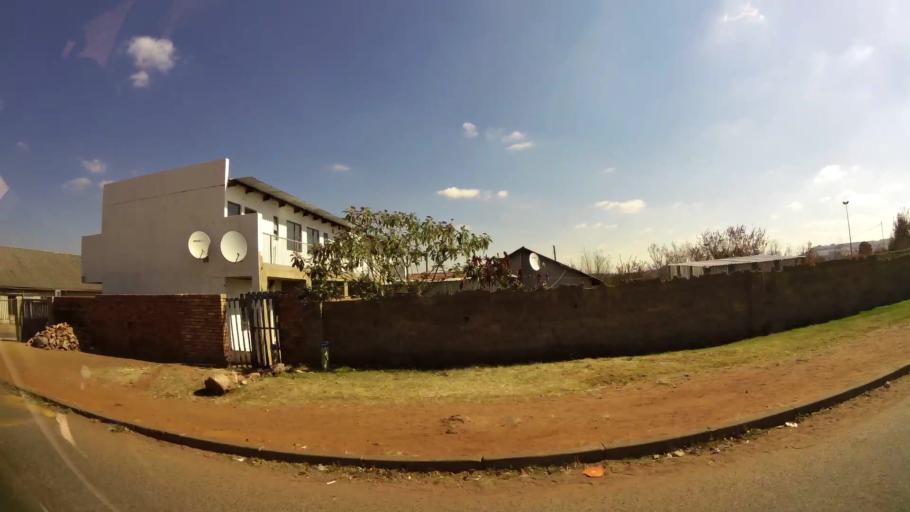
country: ZA
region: Gauteng
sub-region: West Rand District Municipality
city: Krugersdorp
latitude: -26.1503
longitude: 27.7716
